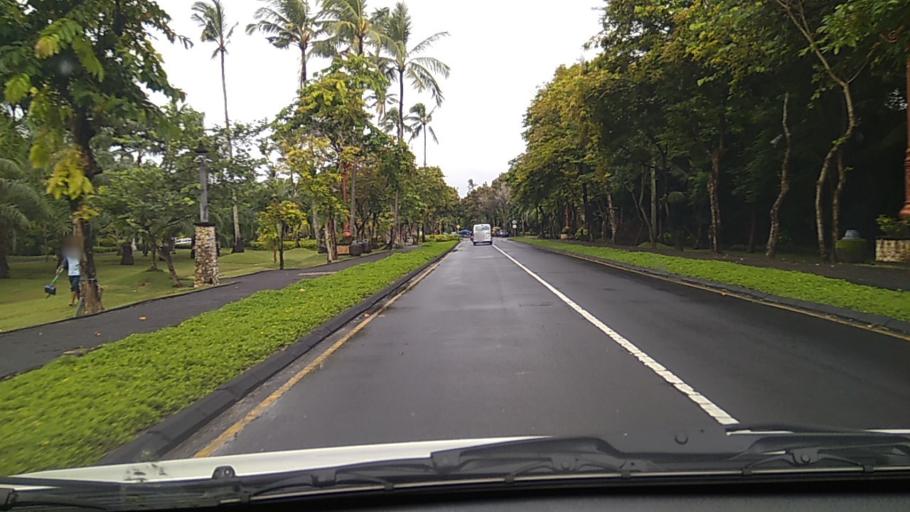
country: ID
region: Bali
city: Bualu
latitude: -8.7941
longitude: 115.2273
